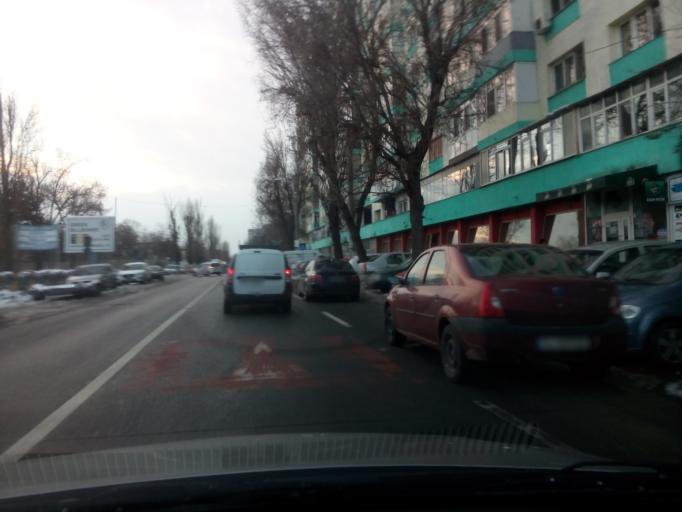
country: RO
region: Ilfov
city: Dobroesti
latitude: 44.4392
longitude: 26.1800
